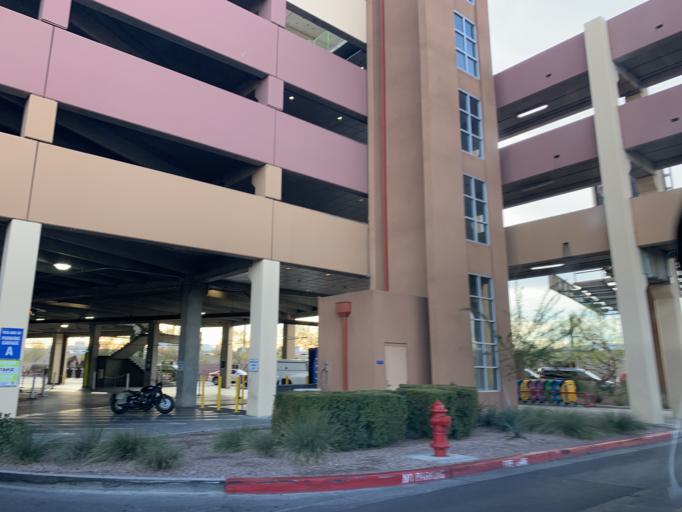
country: US
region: Nevada
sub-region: Clark County
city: Las Vegas
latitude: 36.1622
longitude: -115.1593
